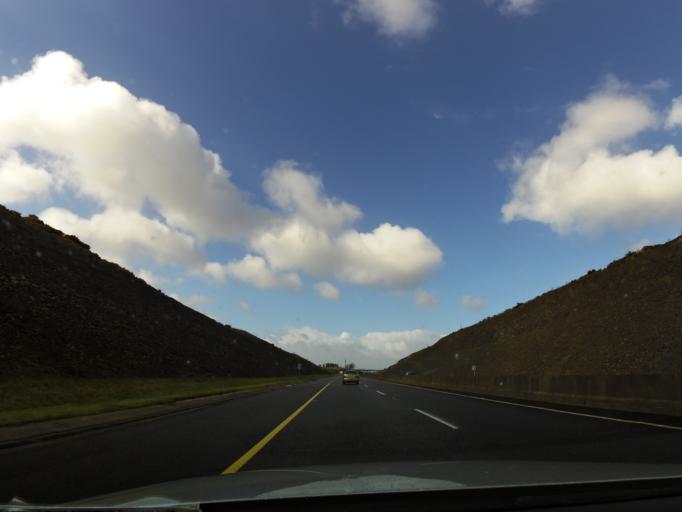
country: IE
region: Munster
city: Ballina
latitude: 52.7698
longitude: -8.3860
